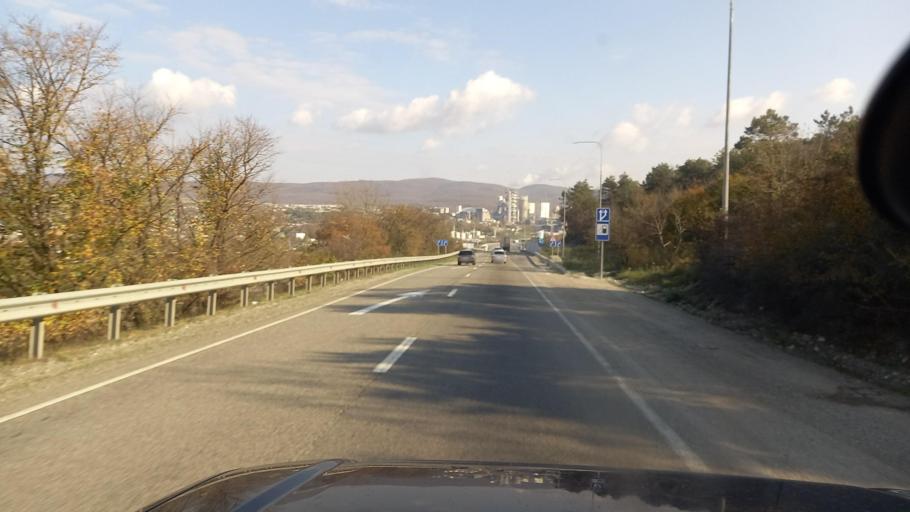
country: RU
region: Krasnodarskiy
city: Verkhnebakanskiy
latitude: 44.8313
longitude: 37.6542
